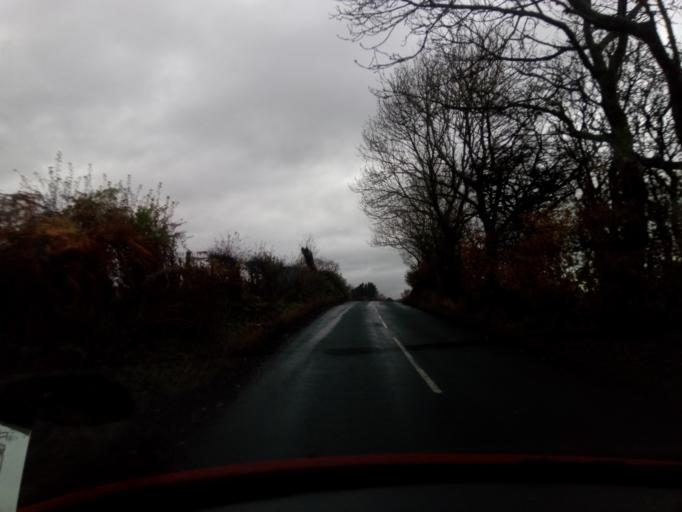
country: GB
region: England
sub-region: County Durham
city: Muggleswick
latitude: 54.8470
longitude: -1.9690
